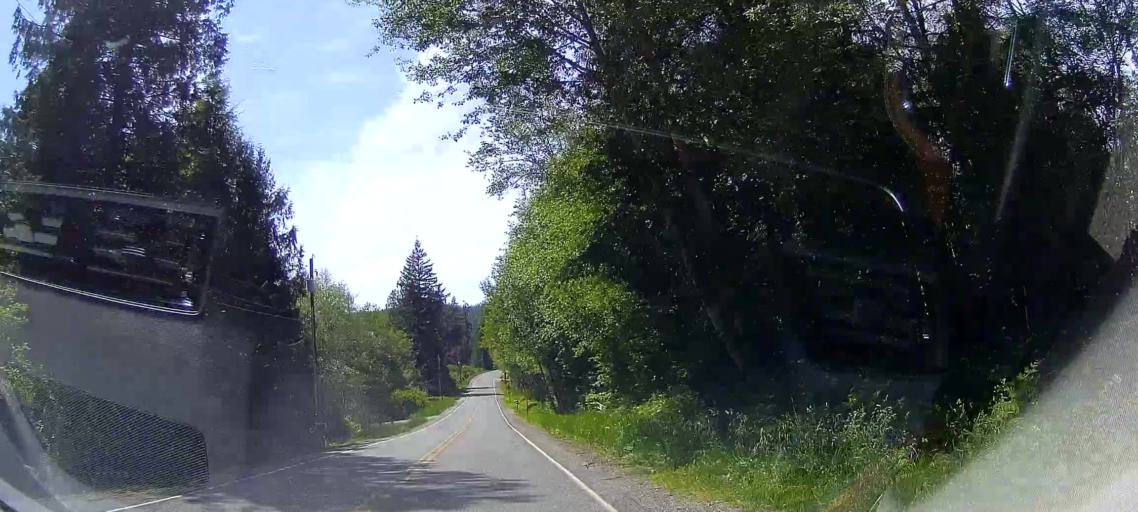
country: US
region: Washington
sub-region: Skagit County
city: Big Lake
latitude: 48.3947
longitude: -122.2793
